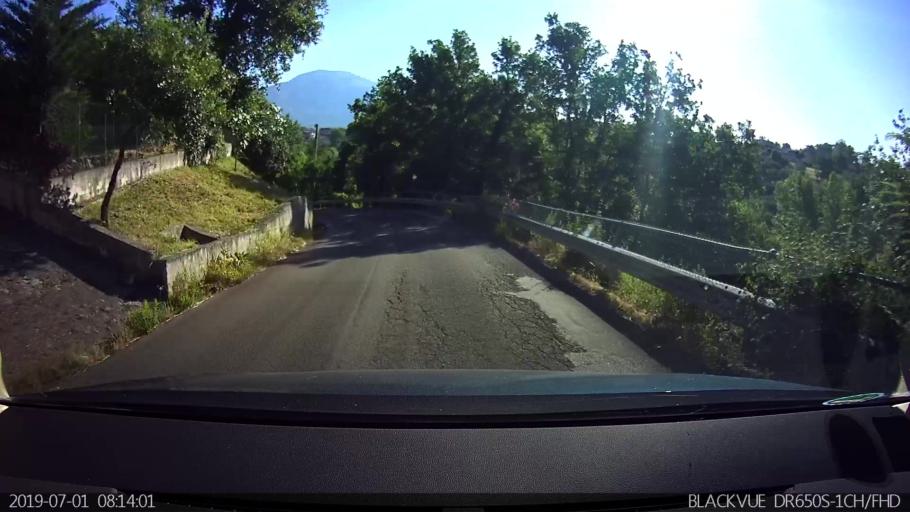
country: IT
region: Latium
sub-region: Provincia di Frosinone
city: Veroli
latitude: 41.6933
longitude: 13.4264
